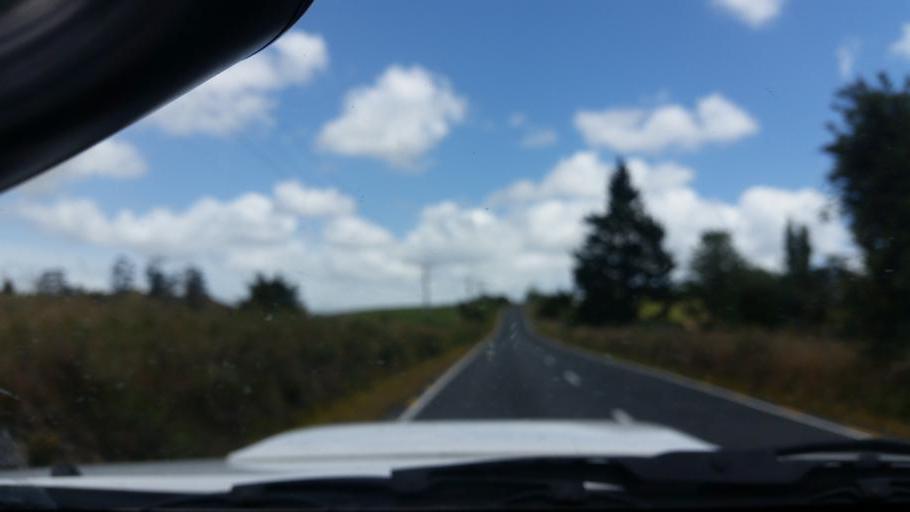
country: NZ
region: Northland
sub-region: Whangarei
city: Ruakaka
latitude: -36.0406
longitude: 174.2794
